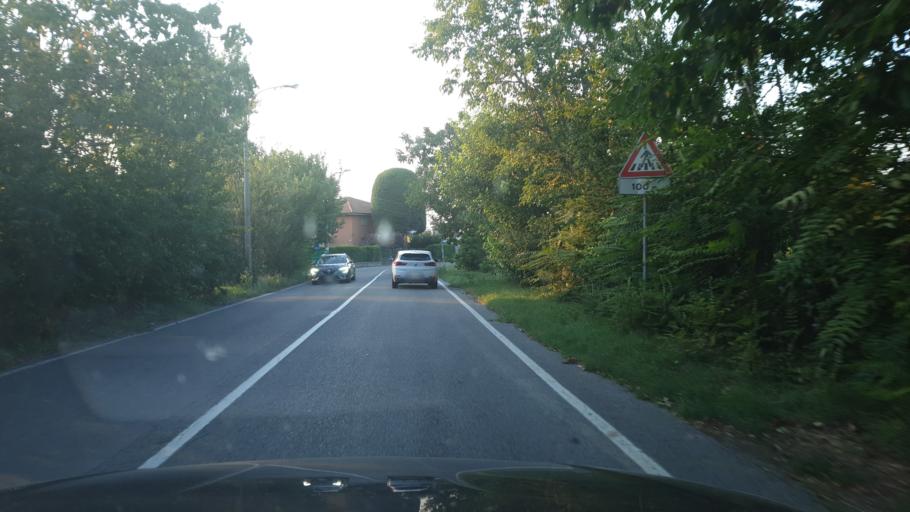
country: IT
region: Emilia-Romagna
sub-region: Provincia di Bologna
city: Quarto Inferiore
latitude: 44.5184
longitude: 11.3816
